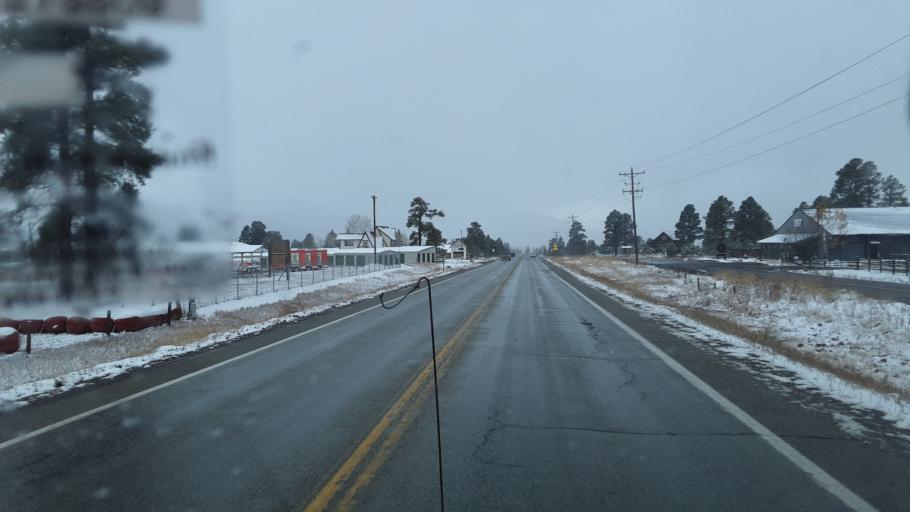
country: US
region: Colorado
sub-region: Archuleta County
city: Pagosa Springs
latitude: 37.2505
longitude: -107.0845
